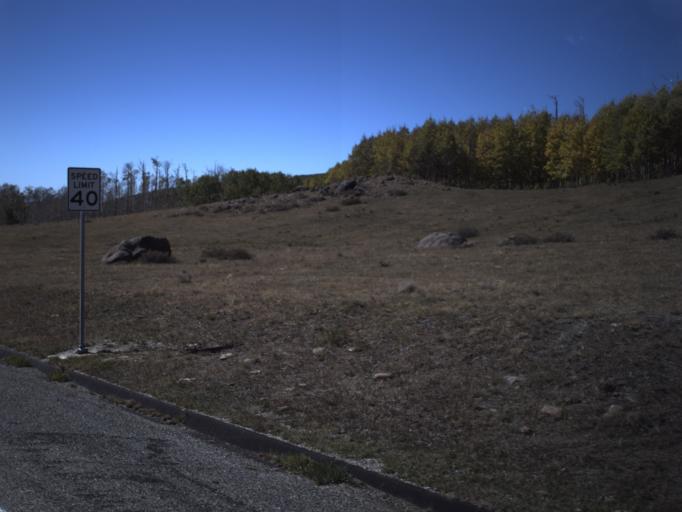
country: US
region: Utah
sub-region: Wayne County
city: Loa
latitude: 38.0358
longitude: -111.3310
